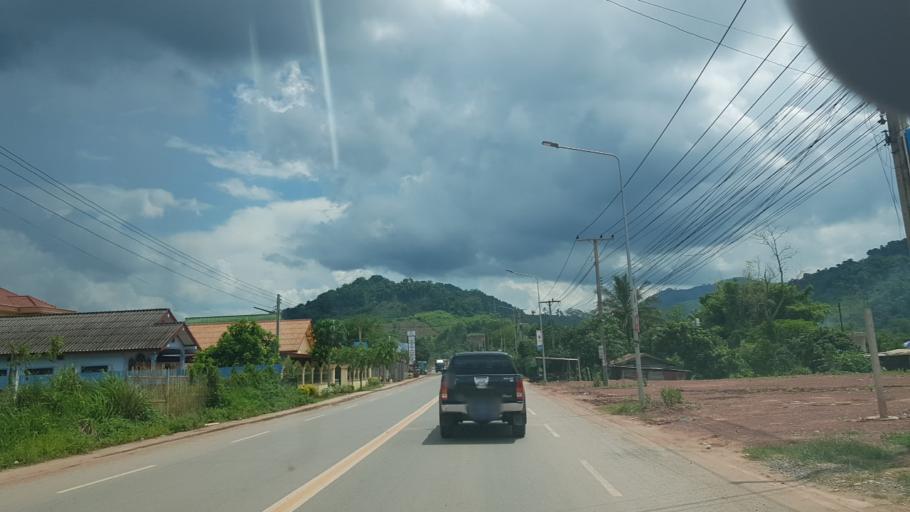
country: LA
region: Oudomxai
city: Muang Xay
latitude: 20.6658
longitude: 101.9794
